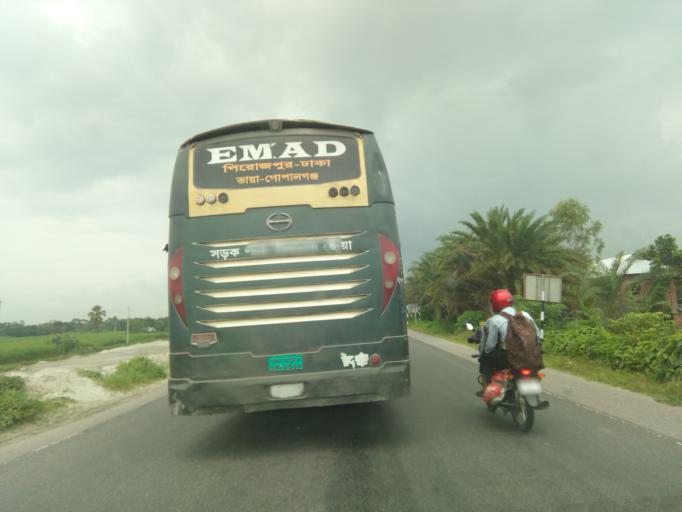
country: BD
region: Dhaka
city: Char Bhadrasan
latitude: 23.3699
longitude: 90.0558
